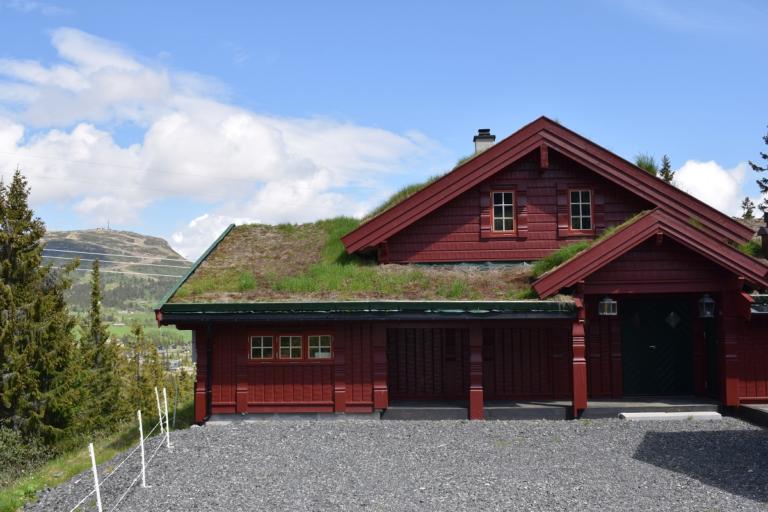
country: NO
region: Oppland
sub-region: Gausdal
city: Segalstad bru
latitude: 61.3310
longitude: 10.0546
